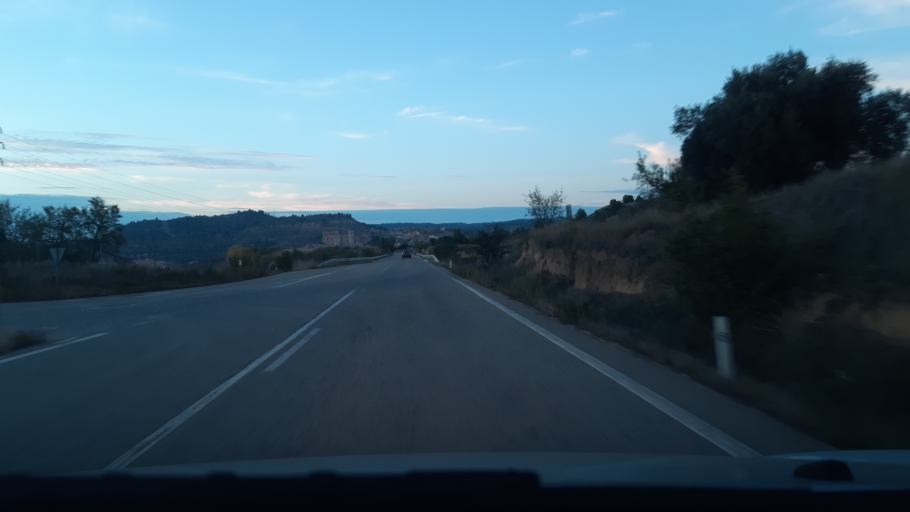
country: ES
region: Aragon
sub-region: Provincia de Teruel
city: Valderrobres
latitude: 40.8664
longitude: 0.1630
